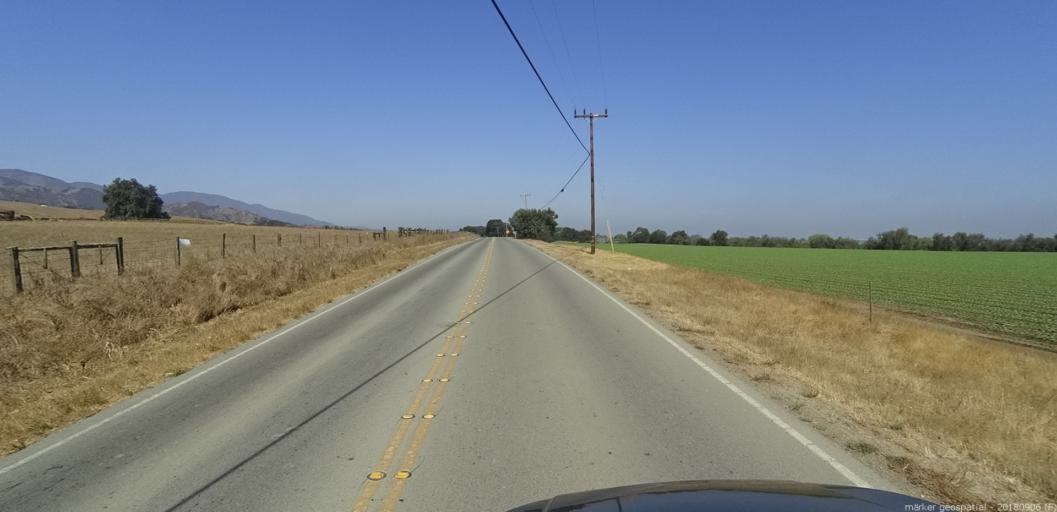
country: US
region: California
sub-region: Monterey County
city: Chualar
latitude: 36.5706
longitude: -121.5711
